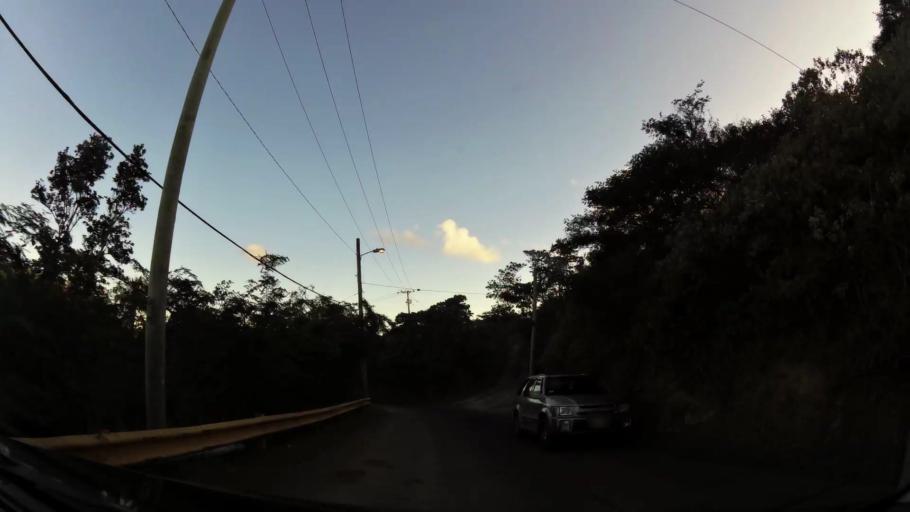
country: VG
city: Road Town
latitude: 18.4400
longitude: -64.6236
